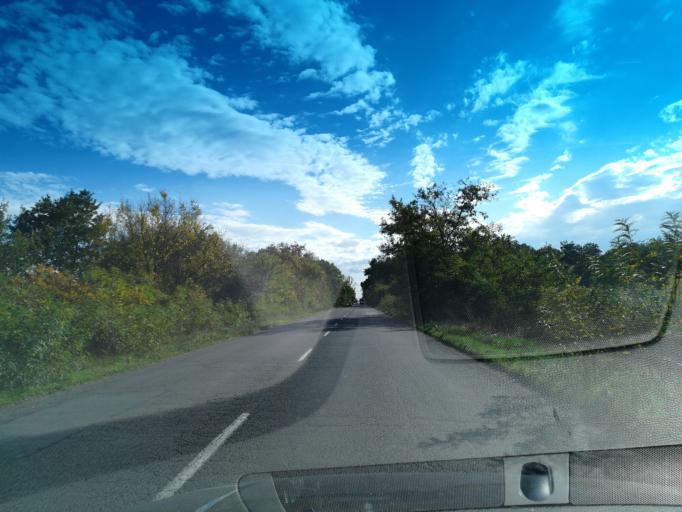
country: BG
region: Stara Zagora
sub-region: Obshtina Stara Zagora
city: Stara Zagora
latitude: 42.3544
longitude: 25.6576
